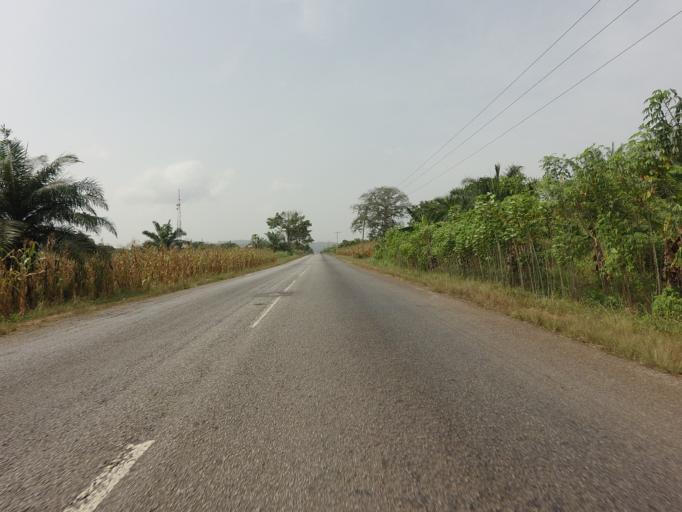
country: GH
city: Akropong
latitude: 6.3072
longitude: 0.1465
